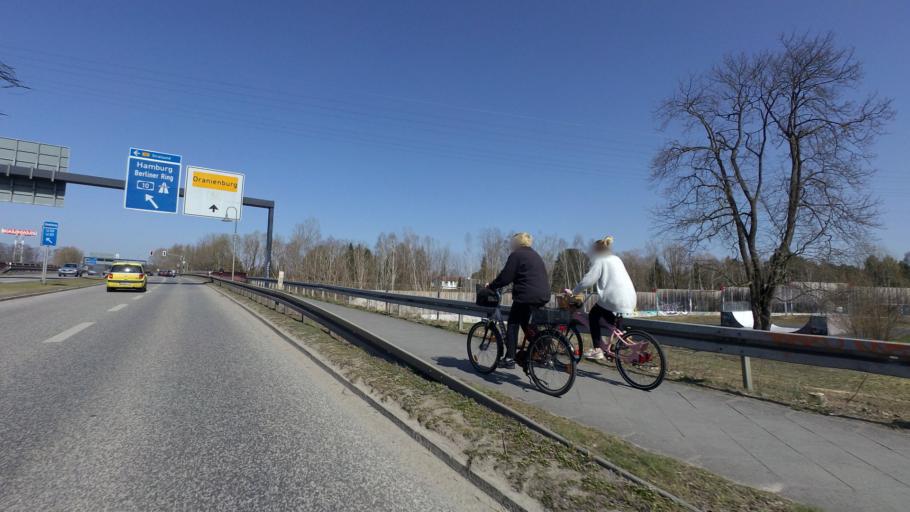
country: DE
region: Brandenburg
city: Birkenwerder
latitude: 52.6993
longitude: 13.2754
